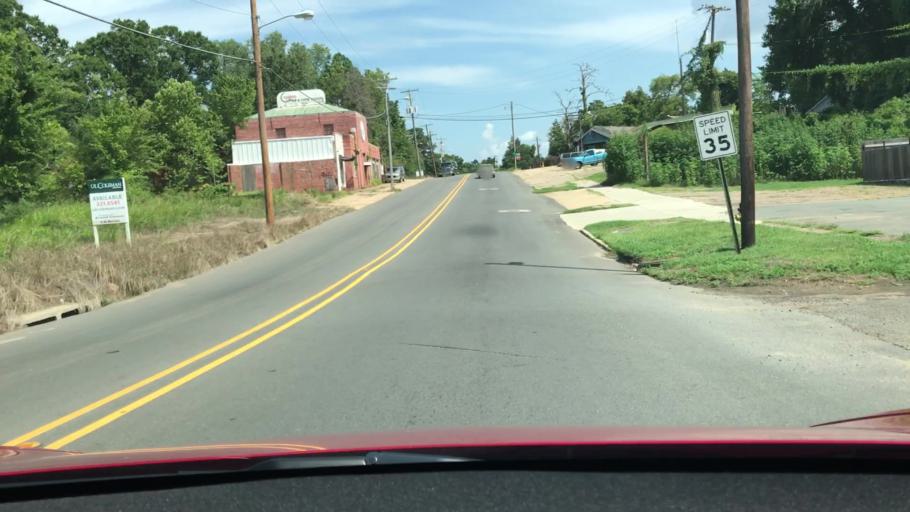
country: US
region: Louisiana
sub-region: Bossier Parish
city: Bossier City
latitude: 32.5027
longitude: -93.7356
